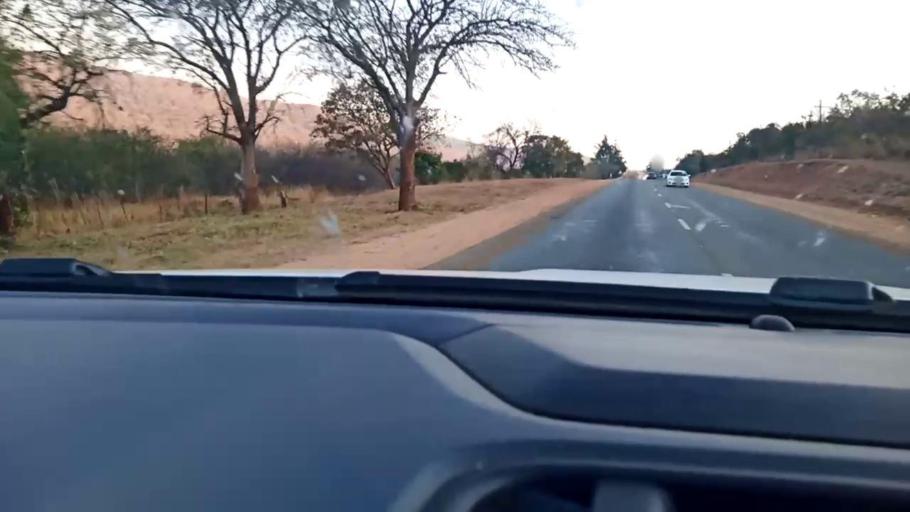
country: ZA
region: Limpopo
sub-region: Mopani District Municipality
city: Duiwelskloof
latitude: -23.6567
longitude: 30.1693
